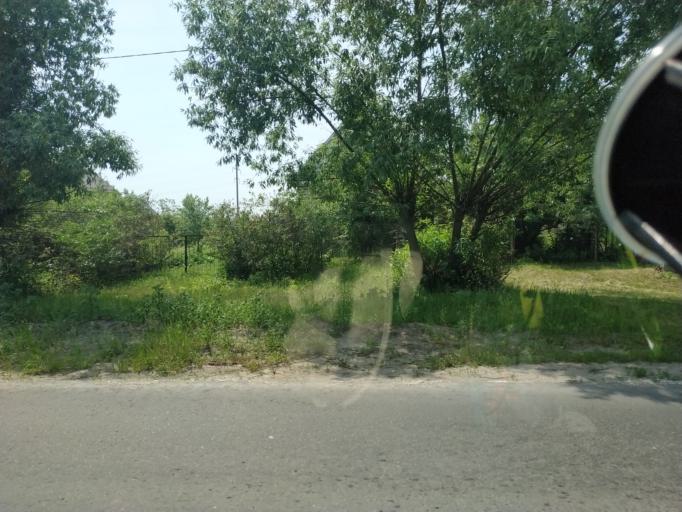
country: RU
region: Moskovskaya
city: Malyshevo
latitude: 55.5013
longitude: 38.3320
